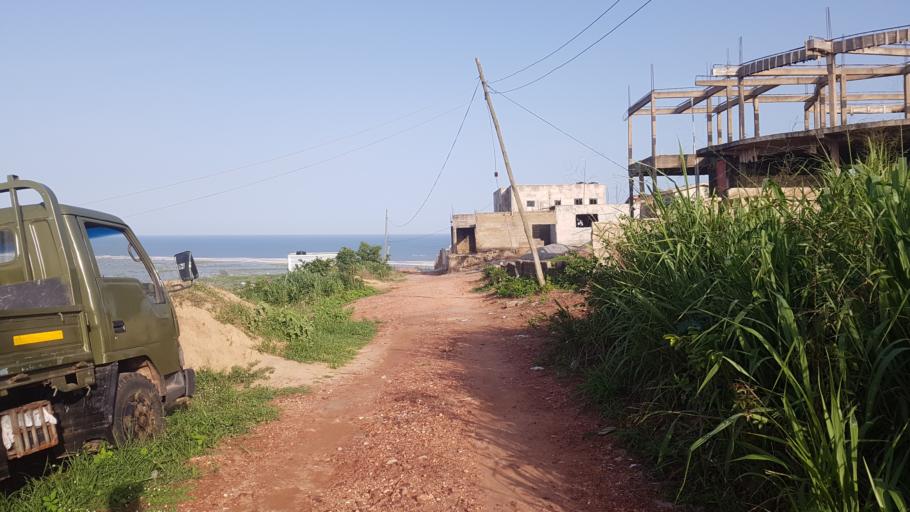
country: GH
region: Greater Accra
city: Gbawe
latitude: 5.5191
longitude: -0.3380
